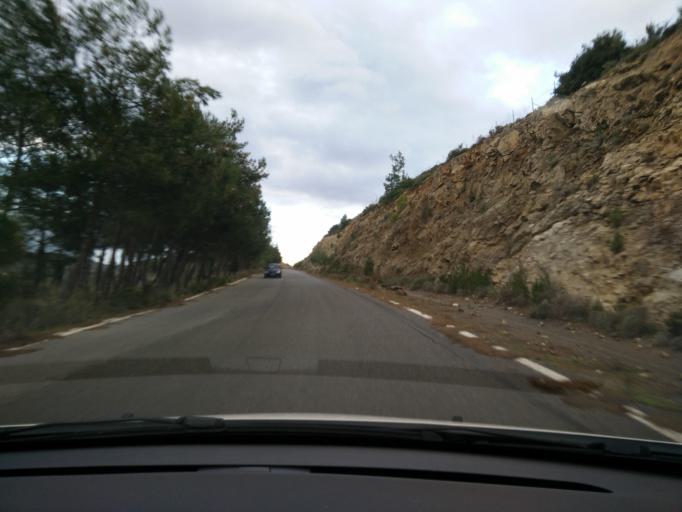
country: GR
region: Crete
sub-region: Nomos Lasithiou
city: Gra Liyia
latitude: 35.0885
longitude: 25.7004
